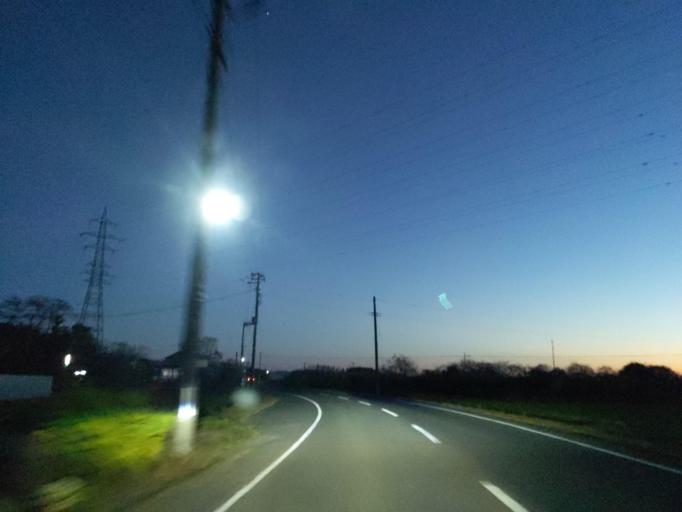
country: JP
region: Fukushima
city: Sukagawa
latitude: 37.3217
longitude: 140.3905
